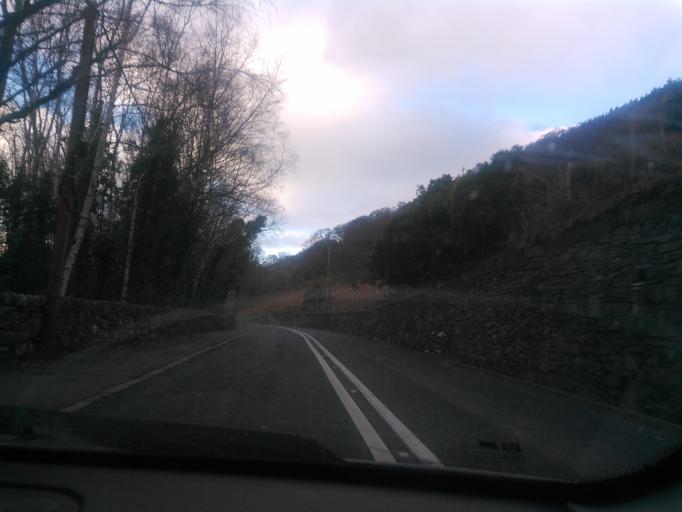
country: GB
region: Wales
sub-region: Gwynedd
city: Bethesda
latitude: 53.1652
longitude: -4.0476
